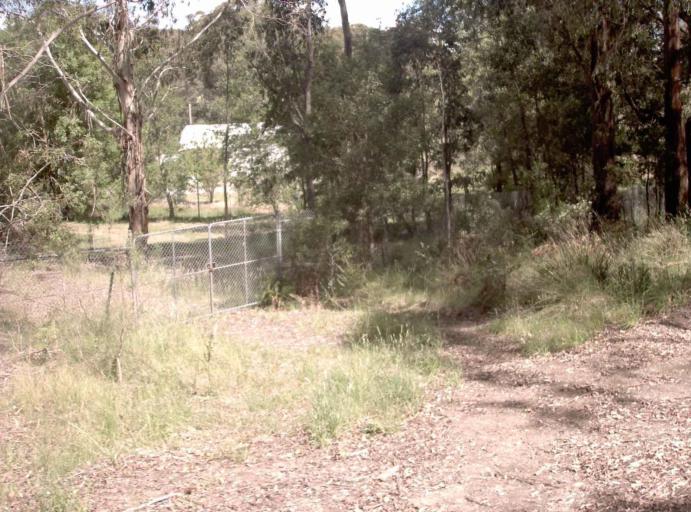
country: AU
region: New South Wales
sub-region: Bombala
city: Bombala
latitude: -37.1871
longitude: 148.7256
